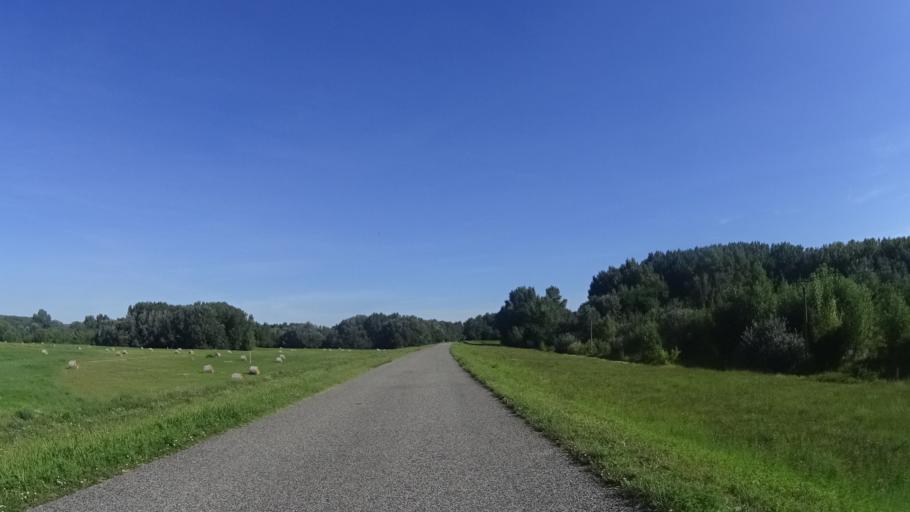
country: SK
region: Bratislavsky
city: Bratislava
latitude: 48.1074
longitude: 17.1465
